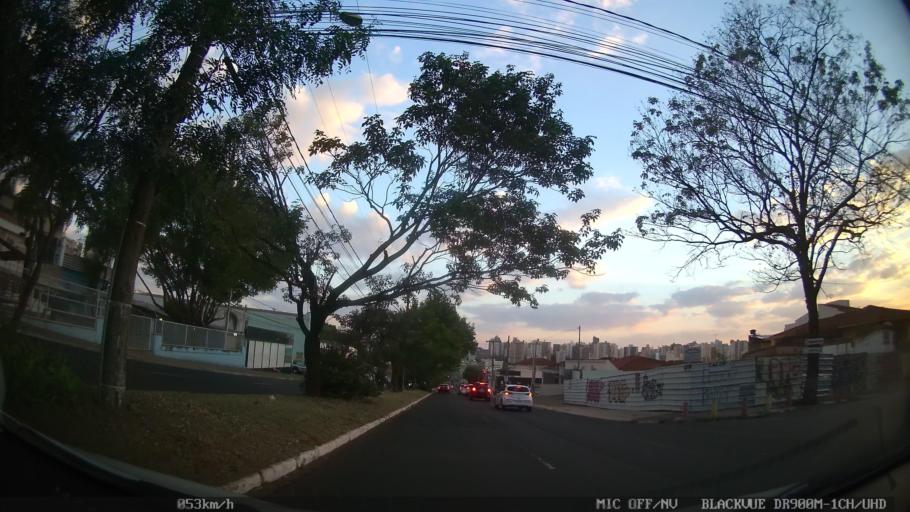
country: BR
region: Sao Paulo
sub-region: Ribeirao Preto
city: Ribeirao Preto
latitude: -21.1759
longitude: -47.7970
